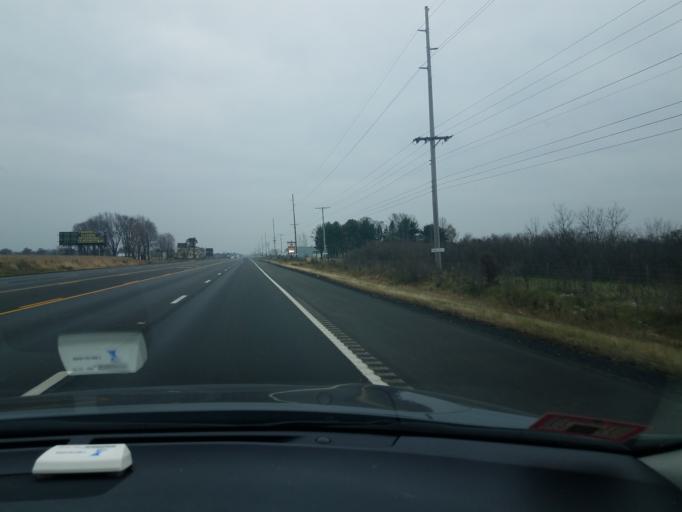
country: US
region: Ohio
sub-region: Erie County
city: Milan
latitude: 41.3705
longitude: -82.6409
